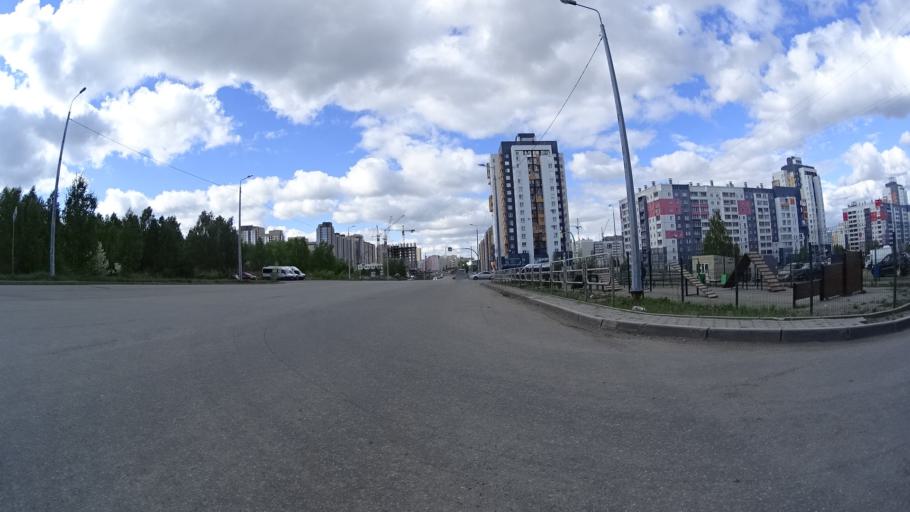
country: RU
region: Chelyabinsk
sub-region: Gorod Chelyabinsk
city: Chelyabinsk
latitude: 55.1626
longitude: 61.2848
